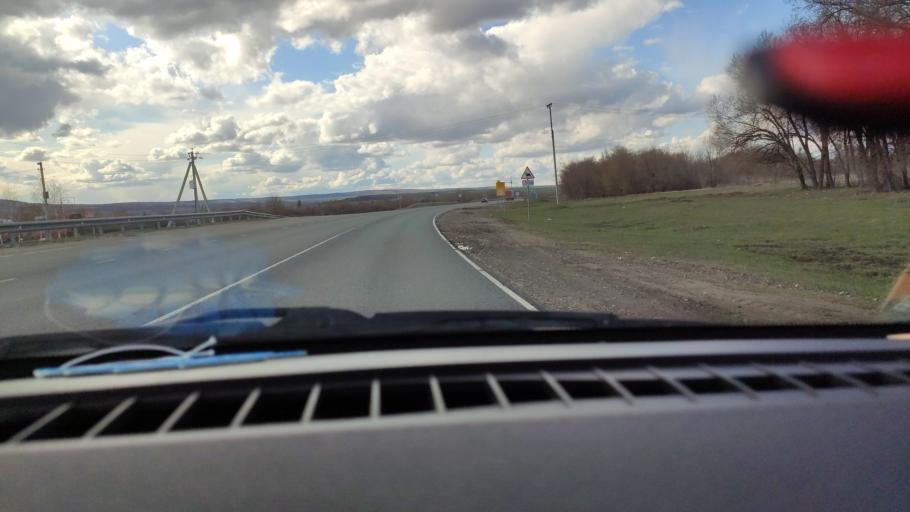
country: RU
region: Saratov
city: Tersa
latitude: 52.0868
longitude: 47.5503
